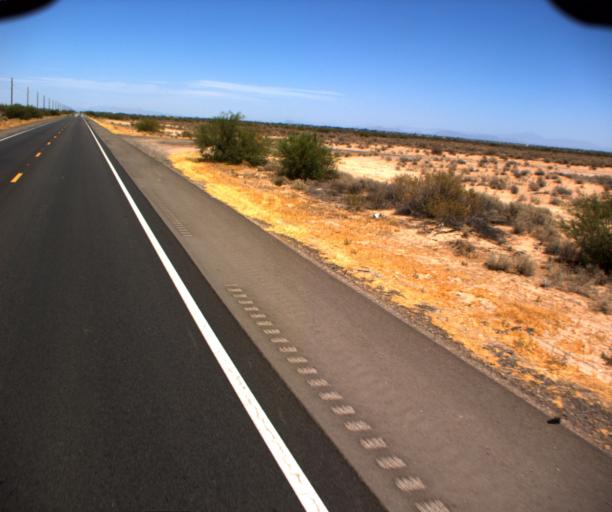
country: US
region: Arizona
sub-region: Maricopa County
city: Sun Lakes
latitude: 33.1719
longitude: -111.8409
